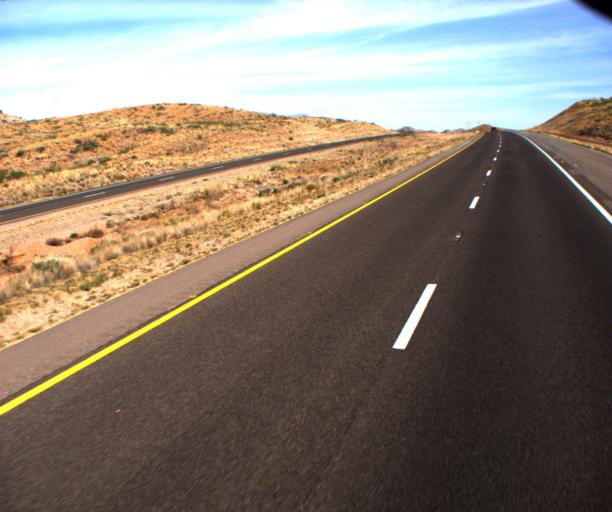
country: US
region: Arizona
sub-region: Cochise County
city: Willcox
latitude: 32.4551
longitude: -109.6648
